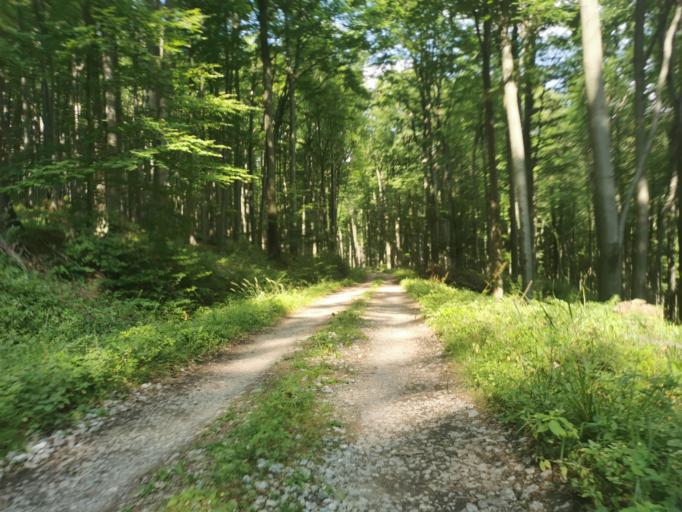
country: SK
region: Trenciansky
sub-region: Okres Myjava
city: Myjava
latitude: 48.8356
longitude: 17.6040
